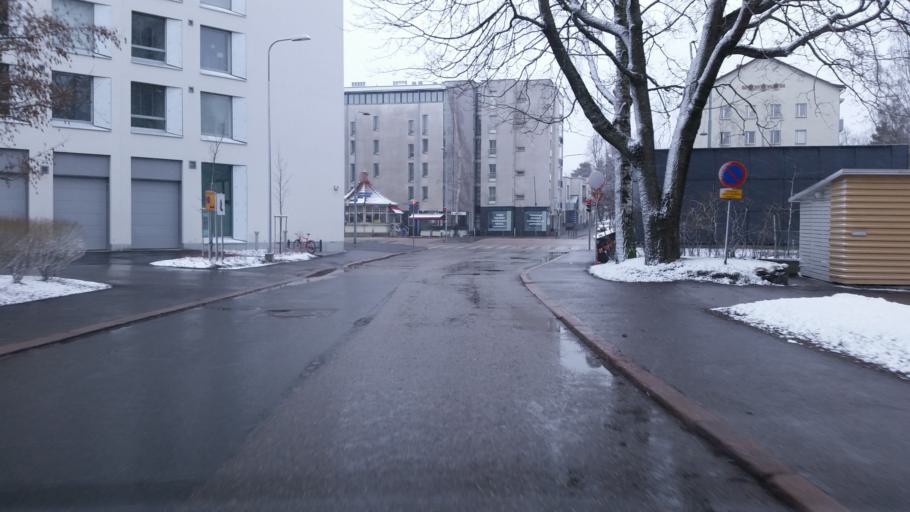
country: FI
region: Uusimaa
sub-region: Helsinki
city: Helsinki
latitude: 60.1620
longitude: 24.8915
